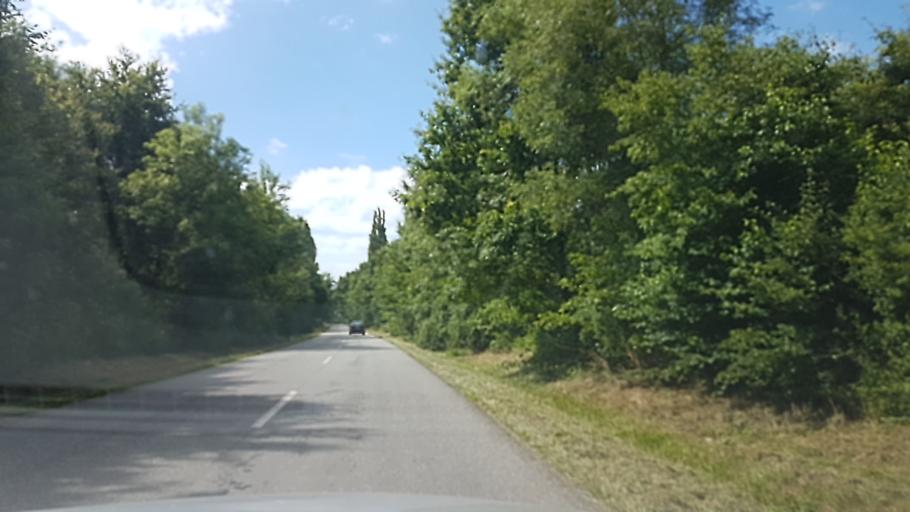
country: HU
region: Somogy
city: Barcs
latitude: 45.9465
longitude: 17.6304
